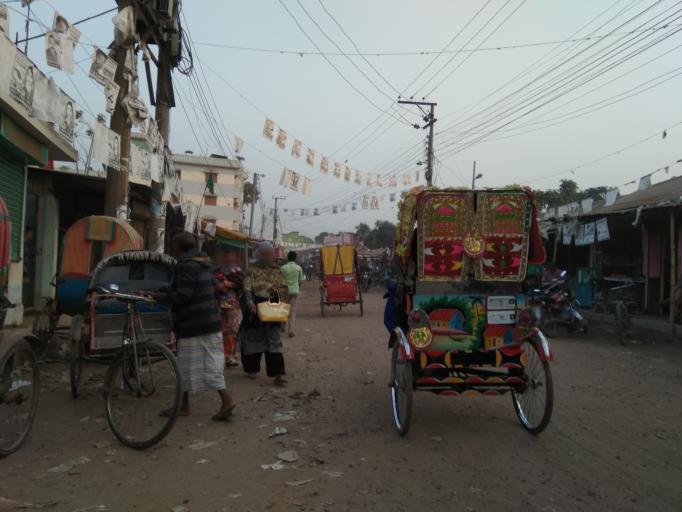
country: BD
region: Rangpur Division
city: Rangpur
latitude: 25.7313
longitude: 89.2645
